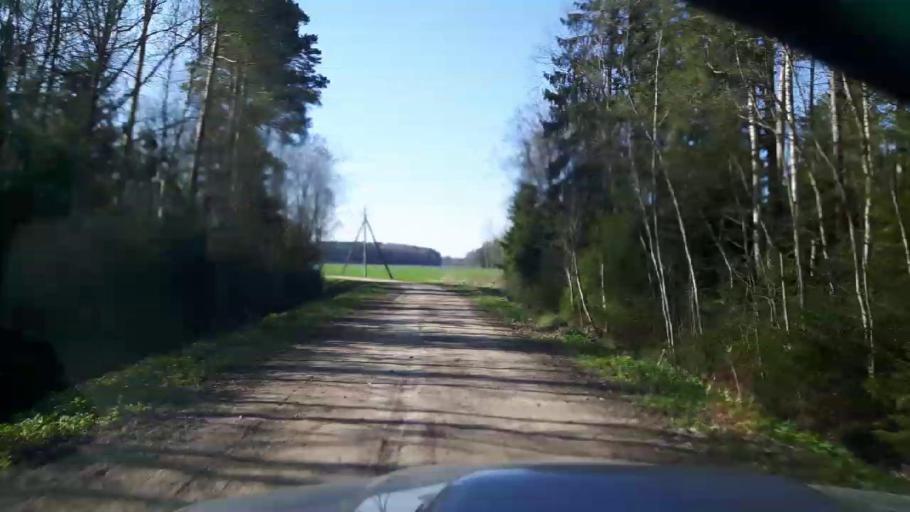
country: EE
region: Paernumaa
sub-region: Tootsi vald
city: Tootsi
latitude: 58.5135
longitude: 24.9297
